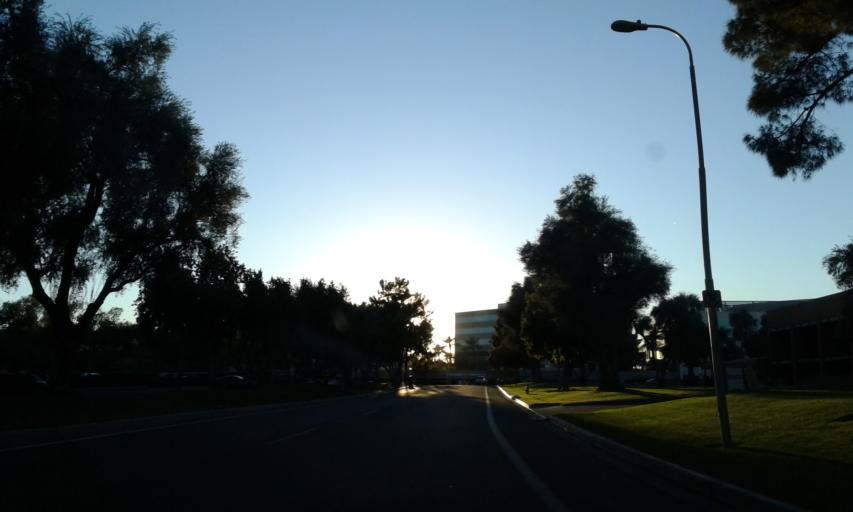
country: US
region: Arizona
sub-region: Maricopa County
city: Glendale
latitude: 33.5692
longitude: -112.1103
